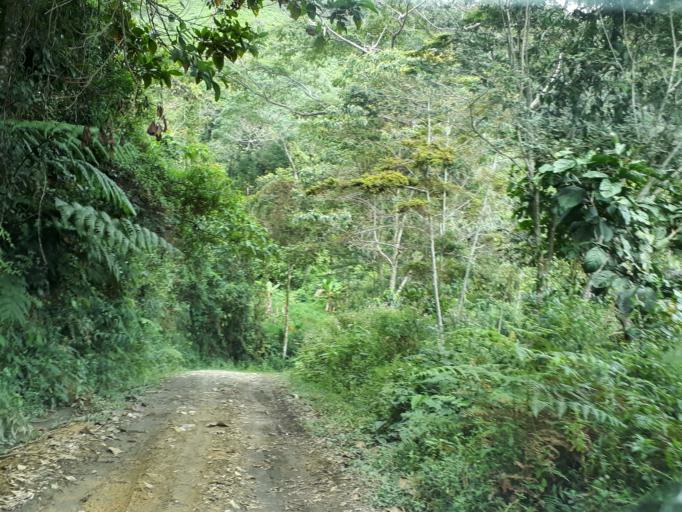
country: CO
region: Boyaca
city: Quipama
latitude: 5.3942
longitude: -74.1208
